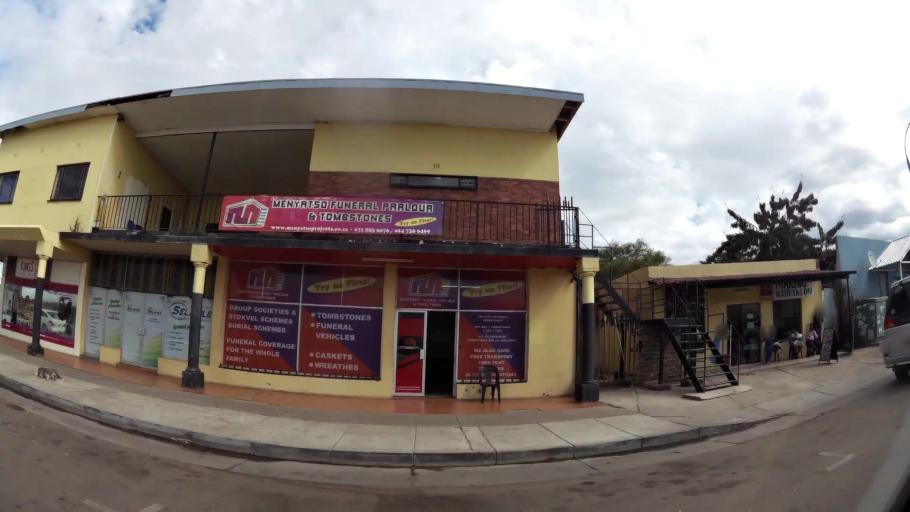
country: ZA
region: Limpopo
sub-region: Waterberg District Municipality
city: Bela-Bela
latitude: -24.8866
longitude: 28.2953
